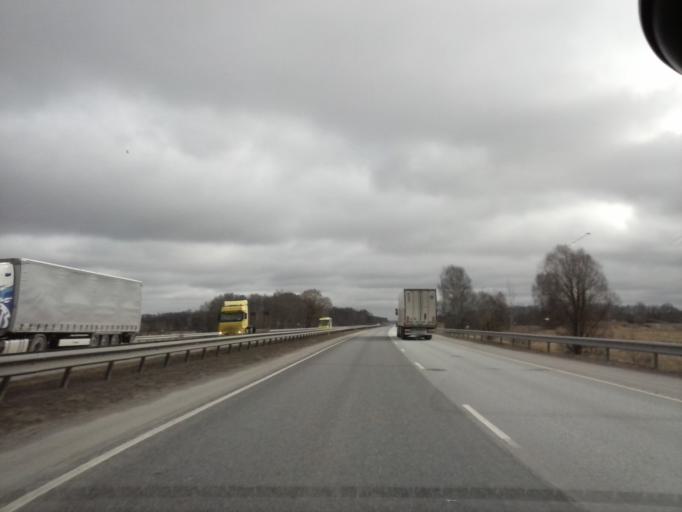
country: EE
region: Harju
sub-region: Rae vald
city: Jueri
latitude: 59.3394
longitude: 24.9033
